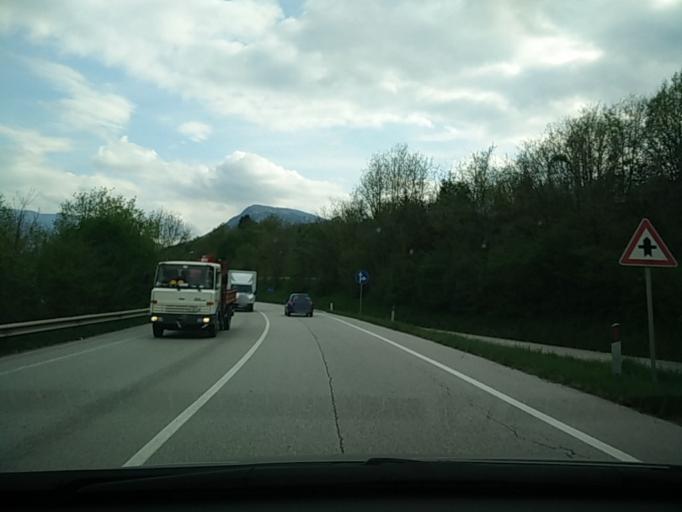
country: IT
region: Veneto
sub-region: Provincia di Belluno
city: Soccher-Paiane-Casan-Arsie
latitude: 46.1592
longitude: 12.3182
